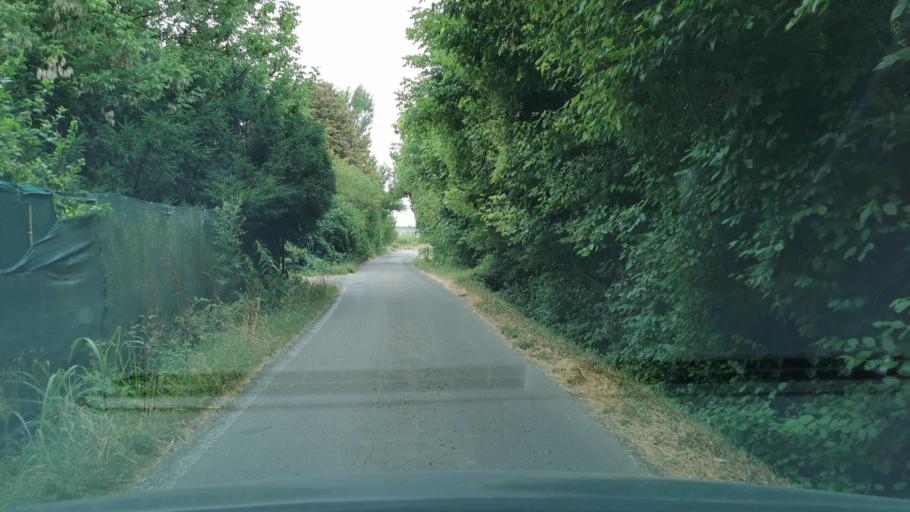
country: IT
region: Emilia-Romagna
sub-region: Provincia di Modena
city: Campogalliano
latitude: 44.6917
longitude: 10.8821
